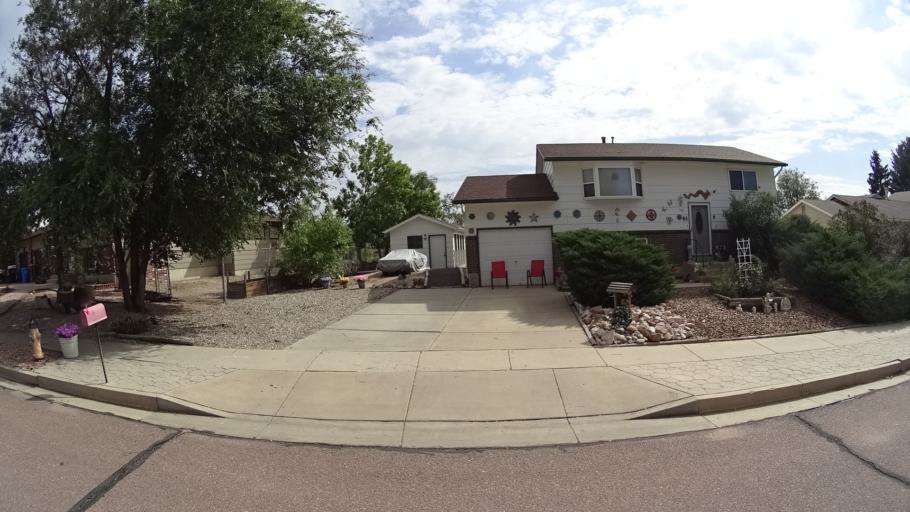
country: US
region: Colorado
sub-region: El Paso County
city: Cimarron Hills
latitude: 38.8489
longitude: -104.7232
